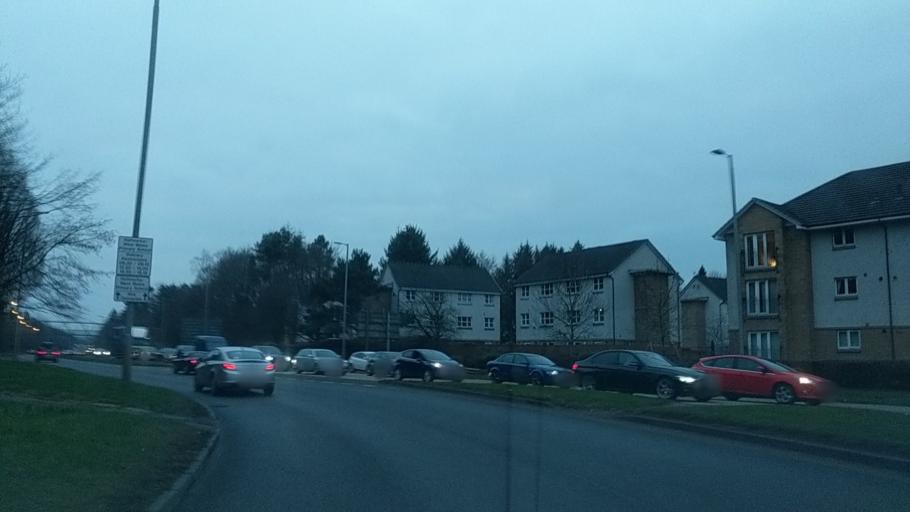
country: GB
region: Scotland
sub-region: South Lanarkshire
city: East Kilbride
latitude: 55.7751
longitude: -4.1631
